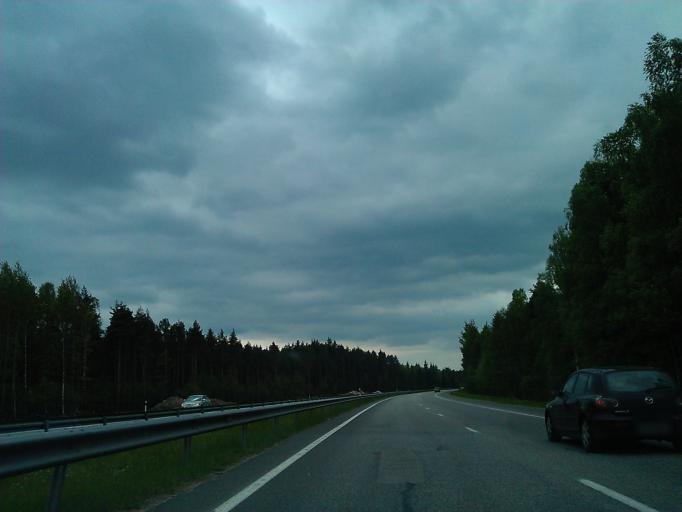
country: LV
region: Marupe
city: Marupe
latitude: 56.8511
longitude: 24.0622
